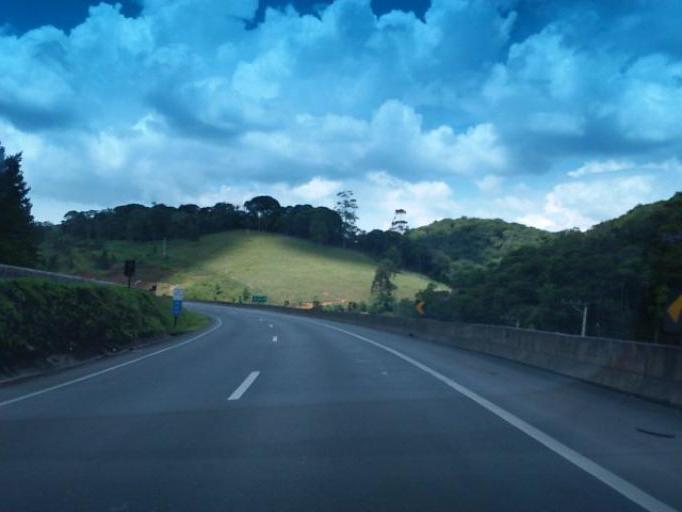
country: BR
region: Sao Paulo
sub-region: Juquitiba
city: Juquitiba
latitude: -24.0035
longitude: -47.1576
